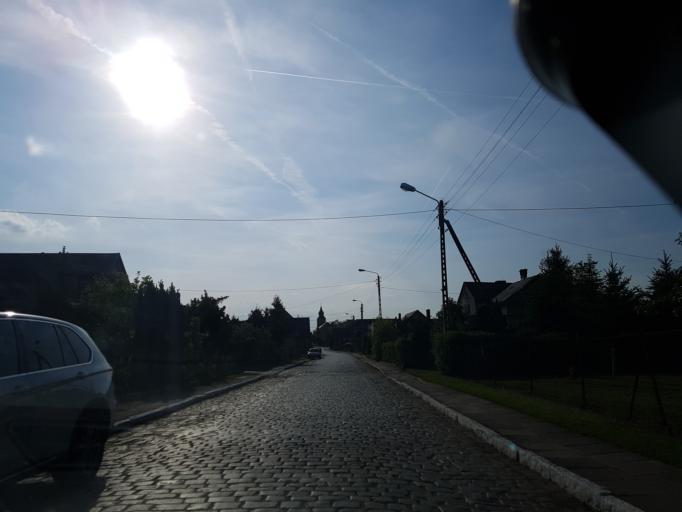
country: PL
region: Lower Silesian Voivodeship
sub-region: Powiat strzelinski
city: Wiazow
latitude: 50.8419
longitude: 17.2146
